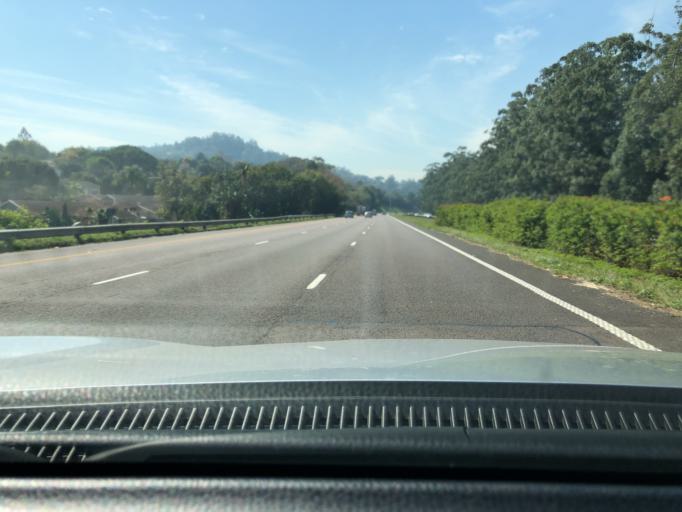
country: ZA
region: KwaZulu-Natal
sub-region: eThekwini Metropolitan Municipality
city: Berea
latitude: -29.8363
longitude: 30.8771
